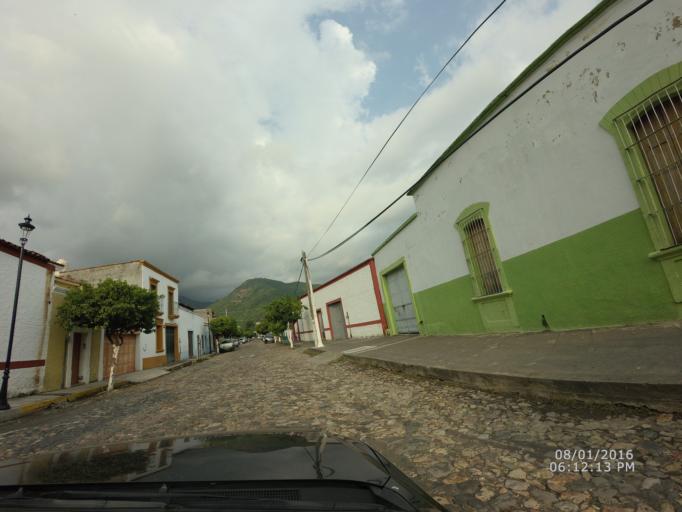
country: MX
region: Nayarit
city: Jala
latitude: 21.1040
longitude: -104.4344
